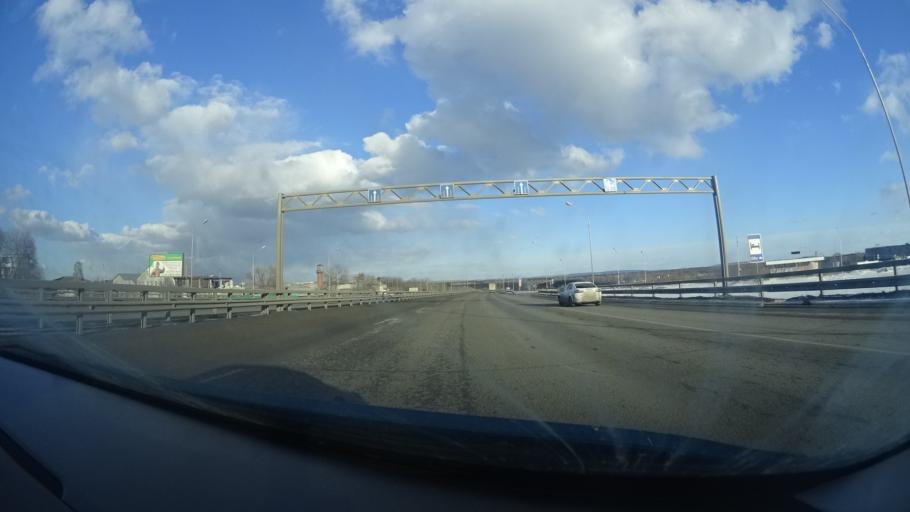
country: RU
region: Bashkortostan
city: Avdon
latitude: 54.6764
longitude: 55.8035
